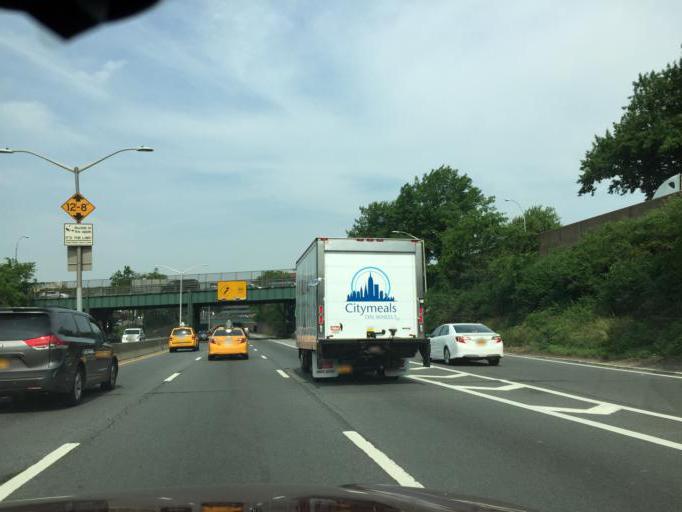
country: US
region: New York
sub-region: Queens County
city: Long Island City
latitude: 40.7696
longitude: -73.9134
